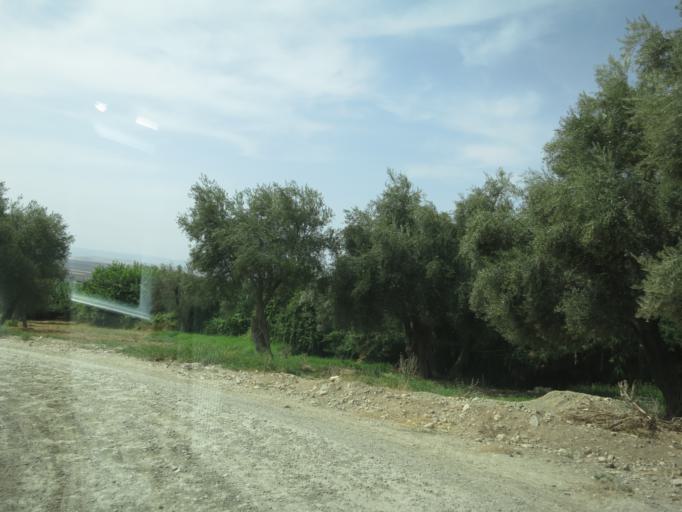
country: MA
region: Meknes-Tafilalet
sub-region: Meknes
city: Meknes
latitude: 34.0735
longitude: -5.5410
